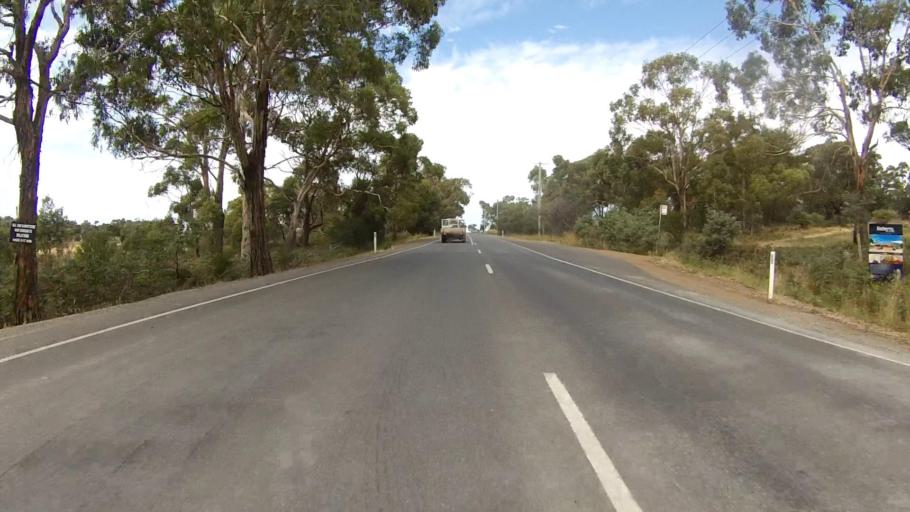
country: AU
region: Tasmania
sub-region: Clarence
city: Sandford
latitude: -42.9442
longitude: 147.4992
